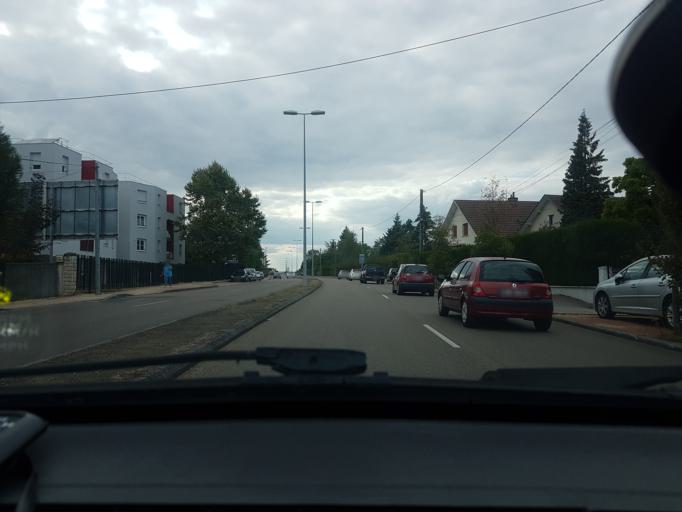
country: FR
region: Bourgogne
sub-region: Departement de la Cote-d'Or
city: Saint-Apollinaire
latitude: 47.3160
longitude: 5.0728
